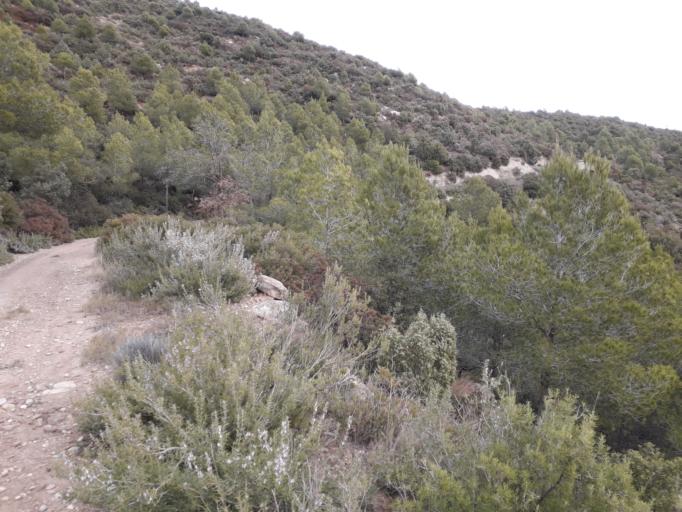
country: ES
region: Catalonia
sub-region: Provincia de Barcelona
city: Jorba
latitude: 41.6404
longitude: 1.5909
